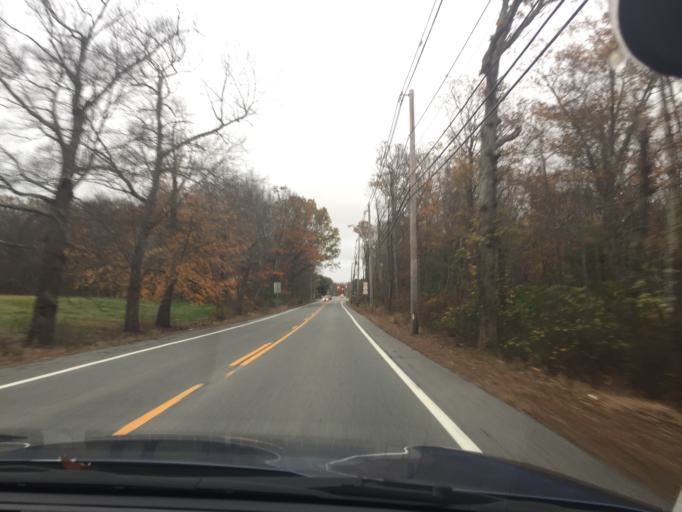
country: US
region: Rhode Island
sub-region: Providence County
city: North Scituate
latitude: 41.8295
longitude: -71.6724
